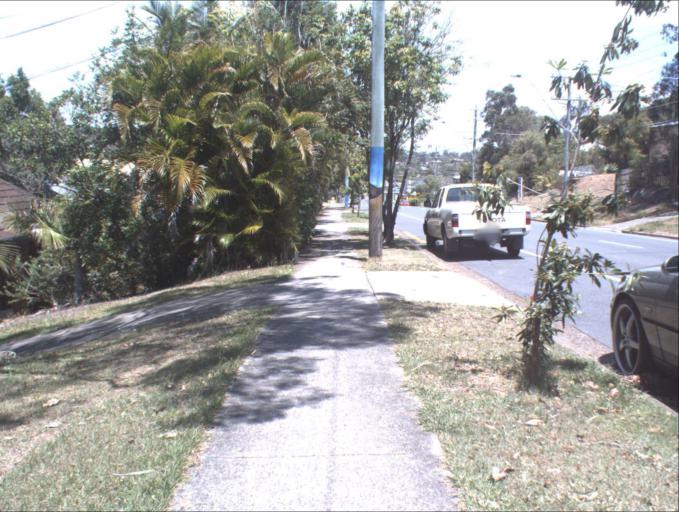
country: AU
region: Queensland
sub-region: Logan
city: Springwood
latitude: -27.6002
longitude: 153.1384
